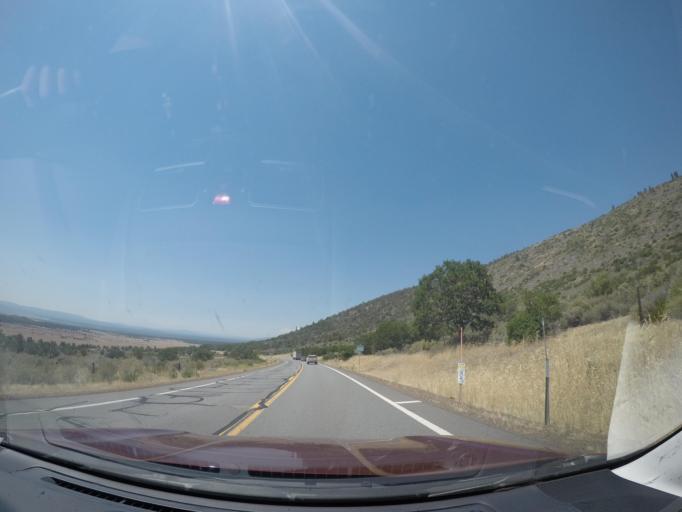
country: US
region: California
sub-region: Shasta County
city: Burney
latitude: 41.0893
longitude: -121.2683
